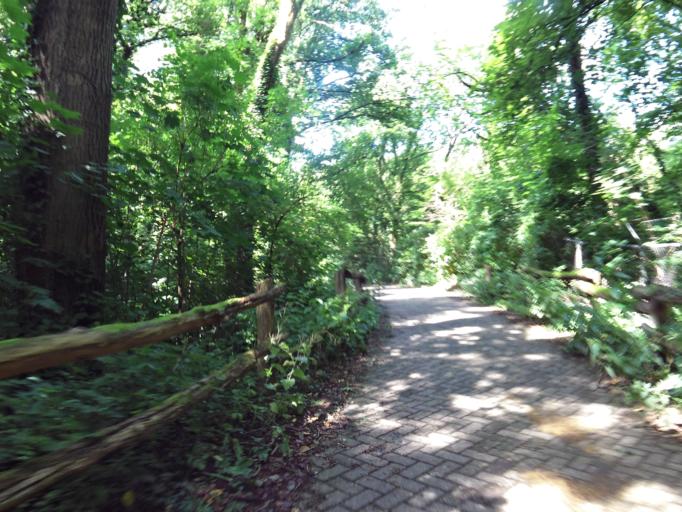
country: NL
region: Limburg
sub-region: Gemeente Kerkrade
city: Kerkrade
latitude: 50.8827
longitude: 6.0310
